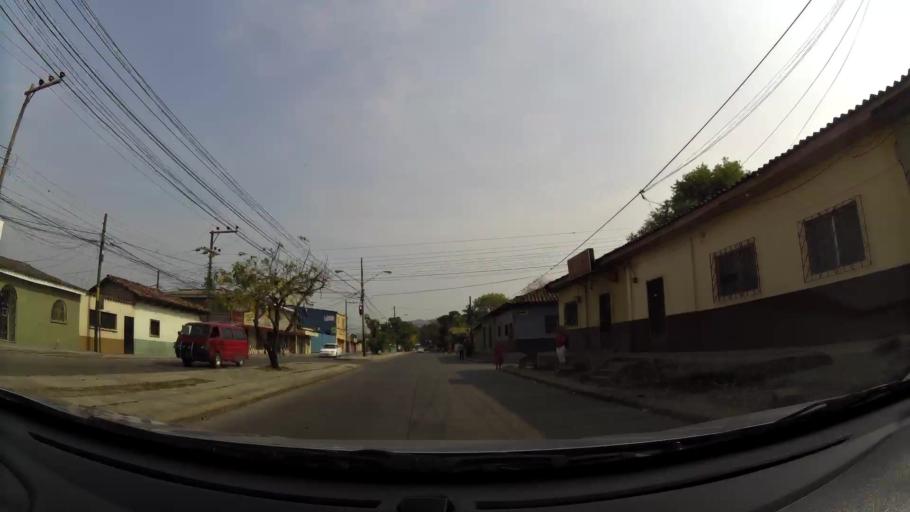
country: HN
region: Comayagua
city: Comayagua
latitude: 14.4620
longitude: -87.6453
